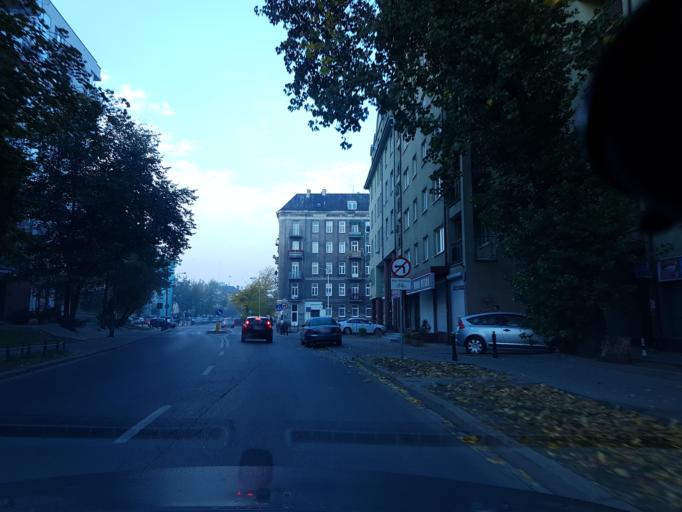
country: PL
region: Masovian Voivodeship
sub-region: Warszawa
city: Praga Polnoc
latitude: 52.2586
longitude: 21.0410
